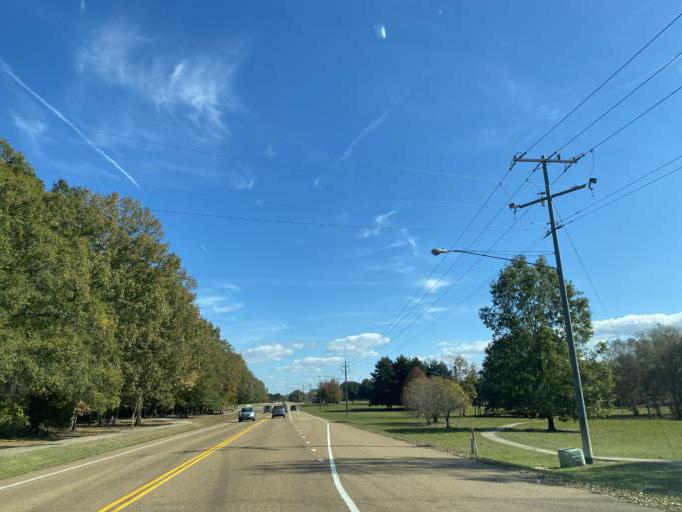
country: US
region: Mississippi
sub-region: Madison County
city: Madison
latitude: 32.4575
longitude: -90.0975
